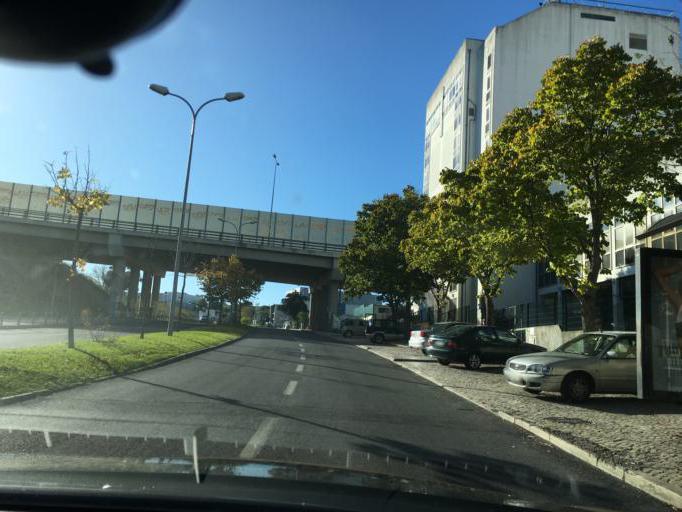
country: PT
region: Lisbon
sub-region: Odivelas
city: Pontinha
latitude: 38.7645
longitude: -9.2097
